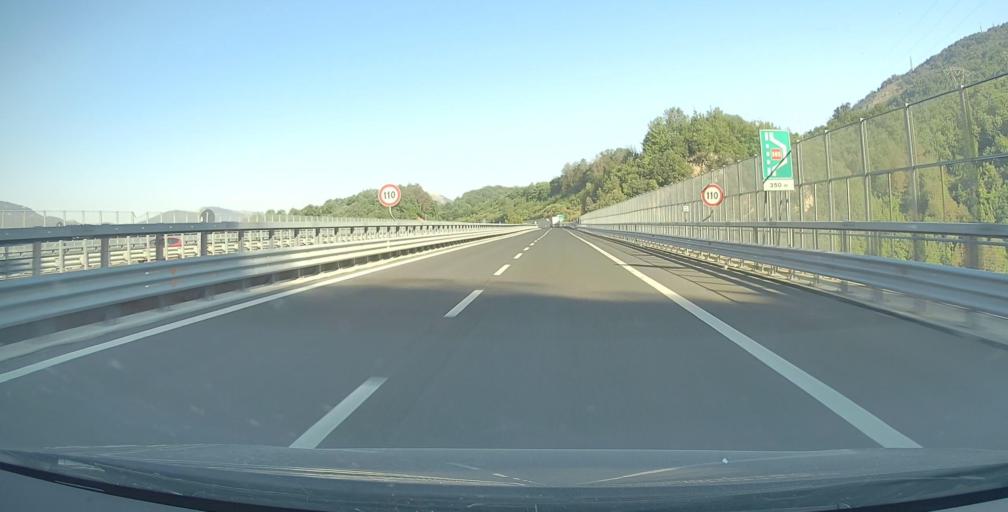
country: IT
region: Basilicate
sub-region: Provincia di Potenza
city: Lagonegro
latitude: 40.1270
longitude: 15.7766
